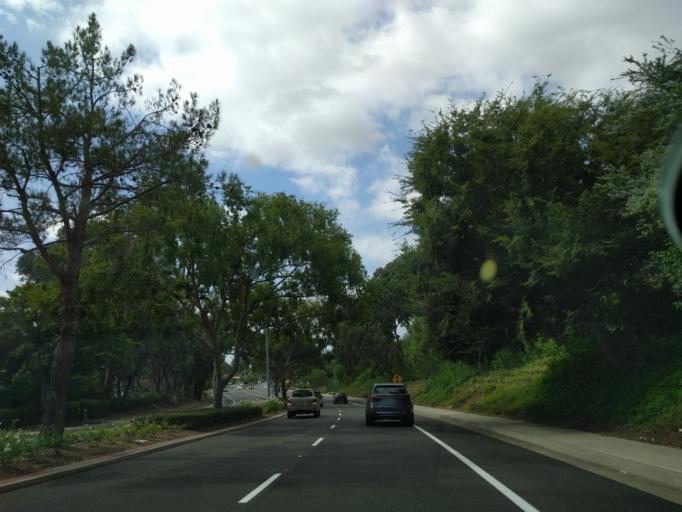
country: US
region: California
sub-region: Orange County
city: Mission Viejo
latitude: 33.6208
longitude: -117.6809
